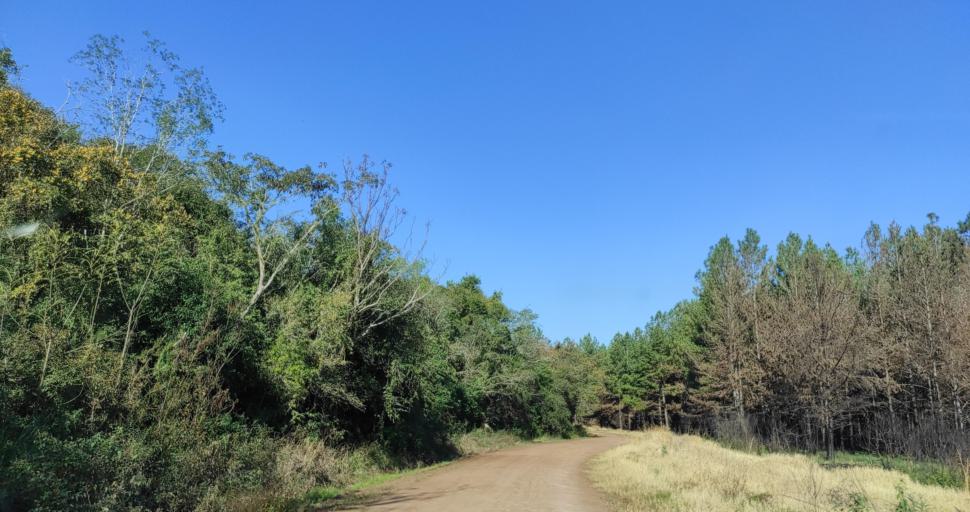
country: AR
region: Misiones
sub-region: Departamento de Apostoles
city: San Jose
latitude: -27.6802
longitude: -55.6545
